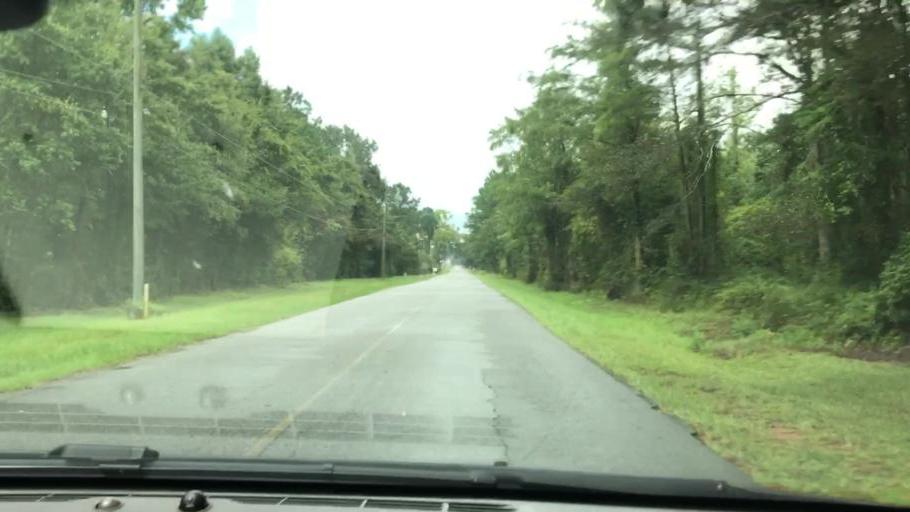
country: US
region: Georgia
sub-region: Early County
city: Blakely
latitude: 31.3667
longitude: -84.9473
